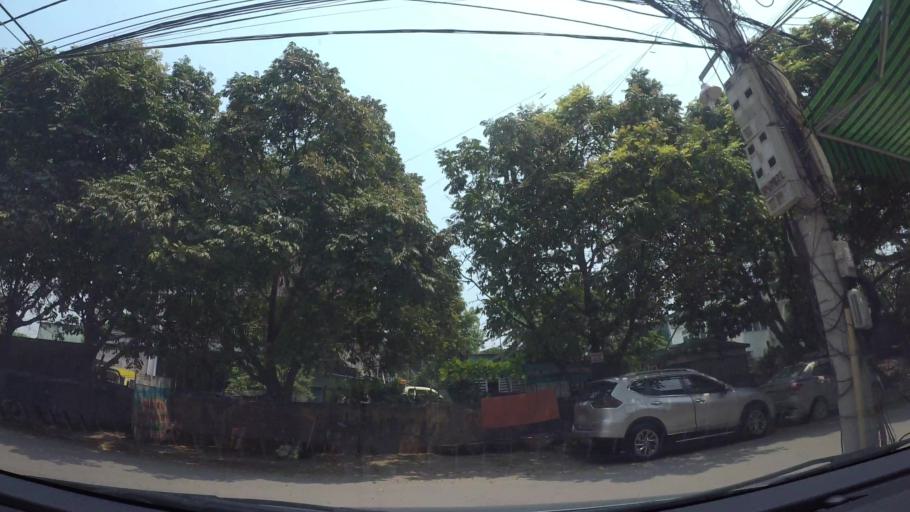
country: VN
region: Ha Noi
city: Thanh Xuan
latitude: 20.9963
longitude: 105.7857
